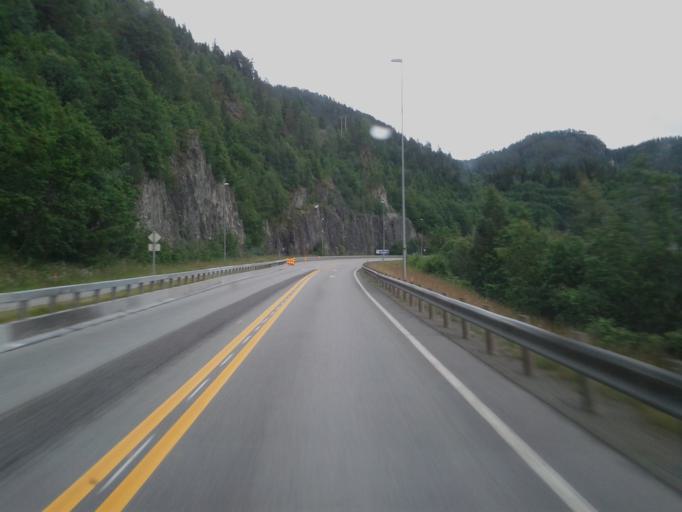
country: NO
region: Sor-Trondelag
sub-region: Midtre Gauldal
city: Storen
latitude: 63.0691
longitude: 10.2801
